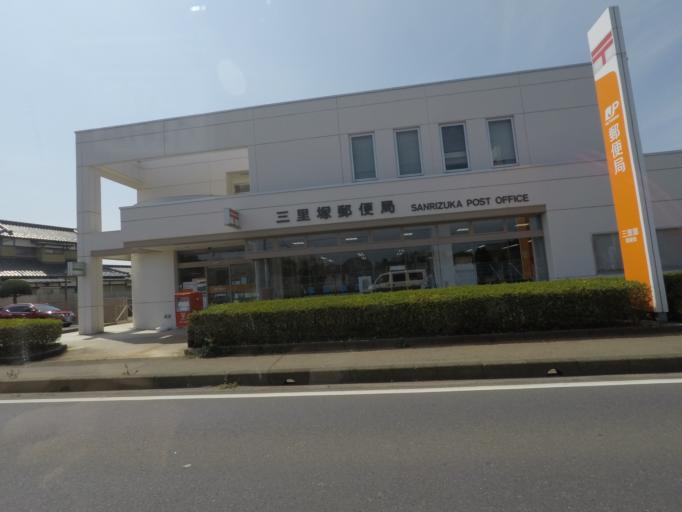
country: JP
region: Chiba
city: Narita
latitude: 35.7645
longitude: 140.3603
